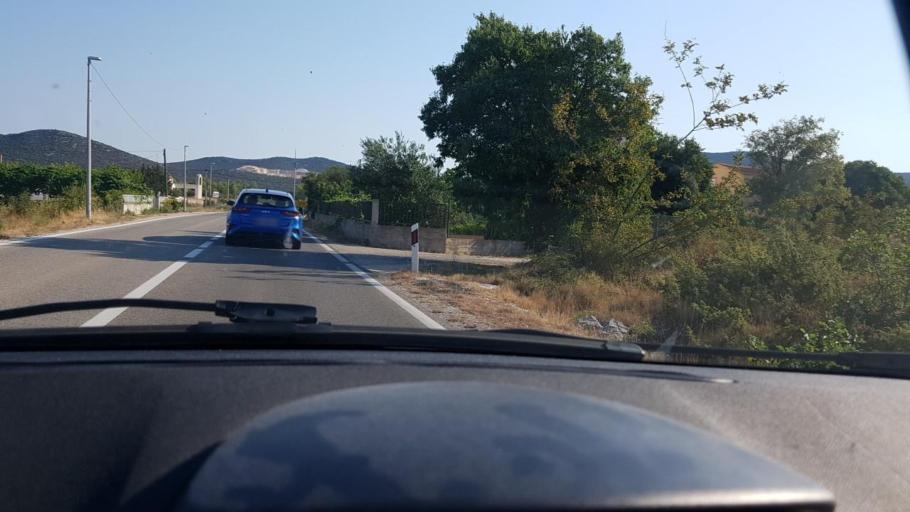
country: HR
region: Sibensko-Kniniska
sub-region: Grad Sibenik
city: Pirovac
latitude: 43.8147
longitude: 15.7071
